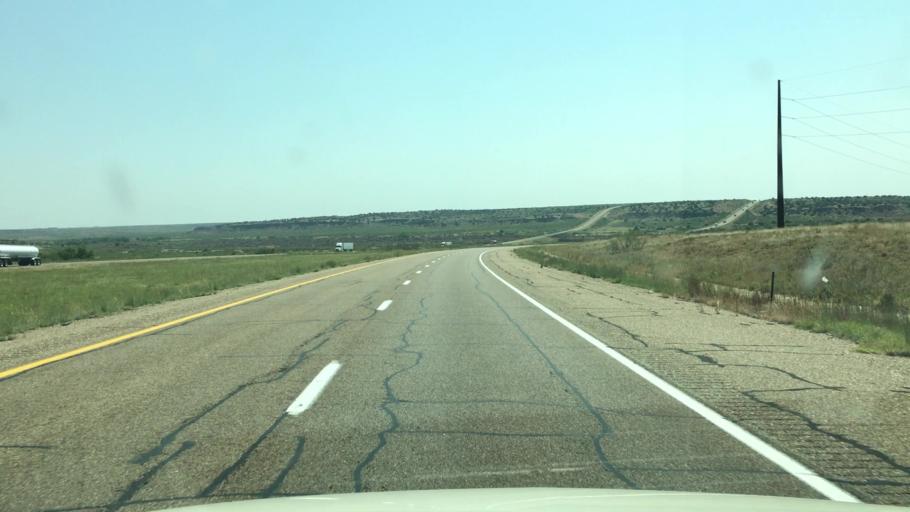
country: US
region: New Mexico
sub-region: Quay County
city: Logan
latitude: 35.1727
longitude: -103.4862
